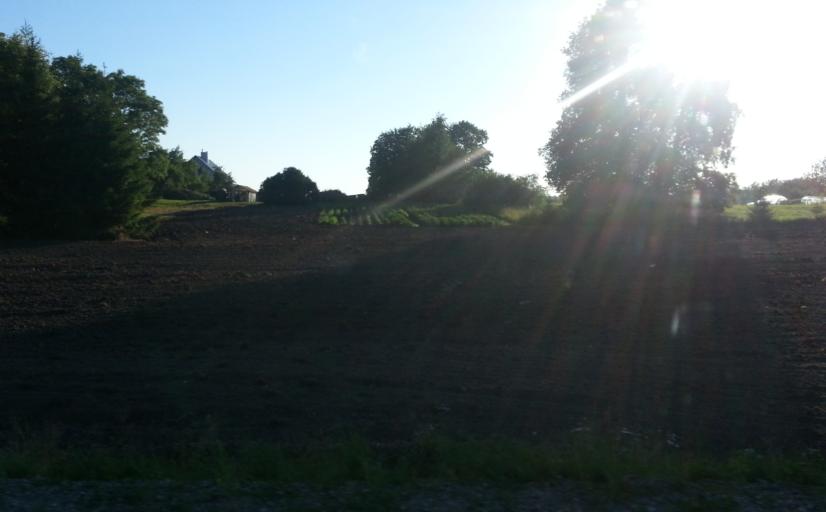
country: LT
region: Panevezys
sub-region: Panevezys City
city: Panevezys
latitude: 55.6291
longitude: 24.3474
